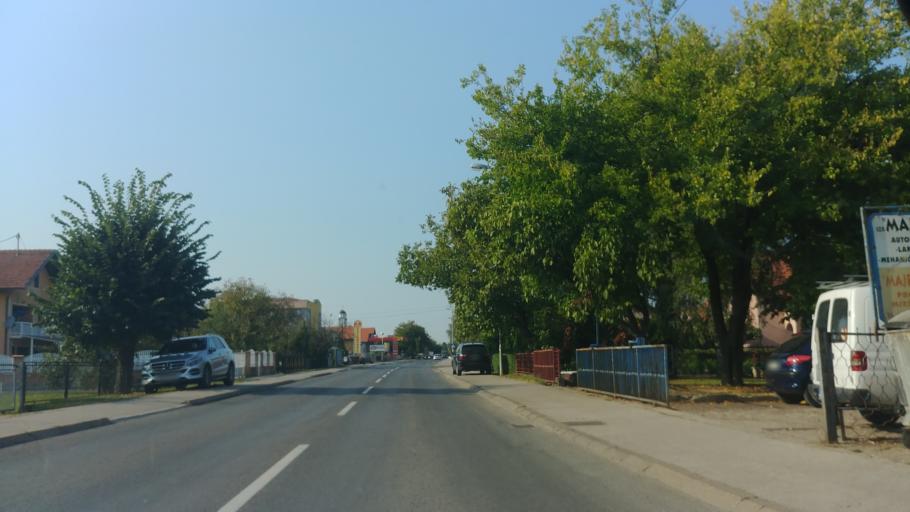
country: BA
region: Brcko
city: Brcko
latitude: 44.8569
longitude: 18.8134
